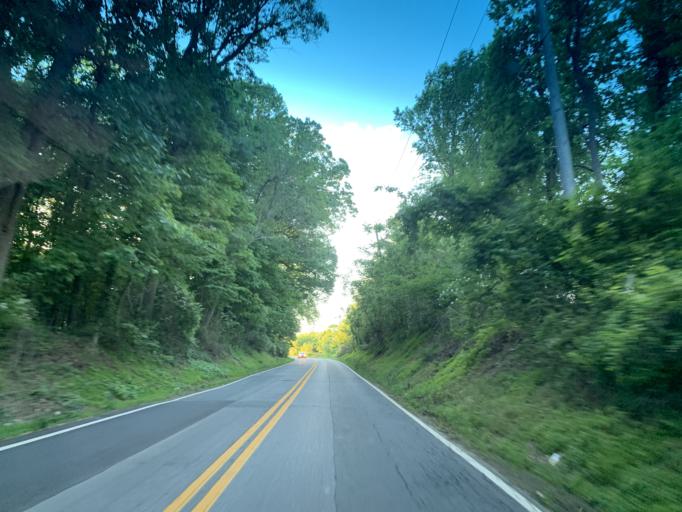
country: US
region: Maryland
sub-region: Cecil County
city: Elkton
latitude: 39.7112
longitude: -75.8693
